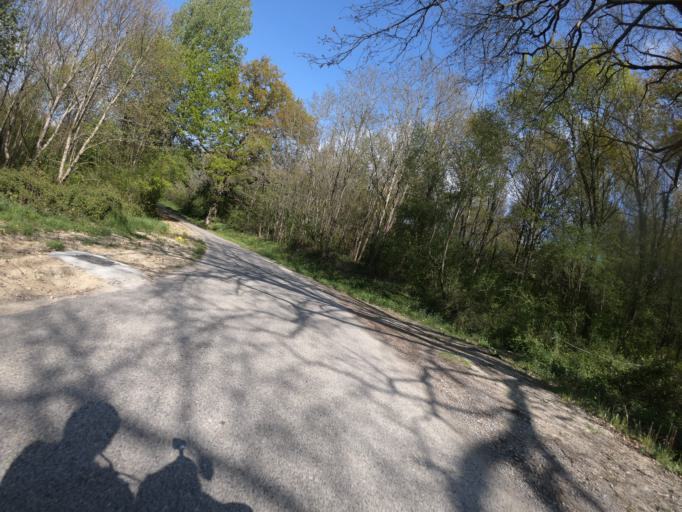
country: FR
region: Midi-Pyrenees
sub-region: Departement de l'Ariege
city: La Tour-du-Crieu
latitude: 43.1062
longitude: 1.6890
